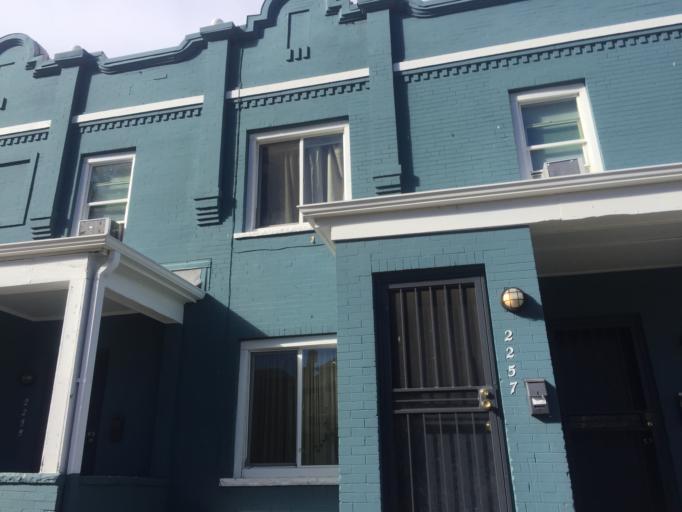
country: US
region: Colorado
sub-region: Denver County
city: Denver
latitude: 39.7507
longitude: -104.9758
